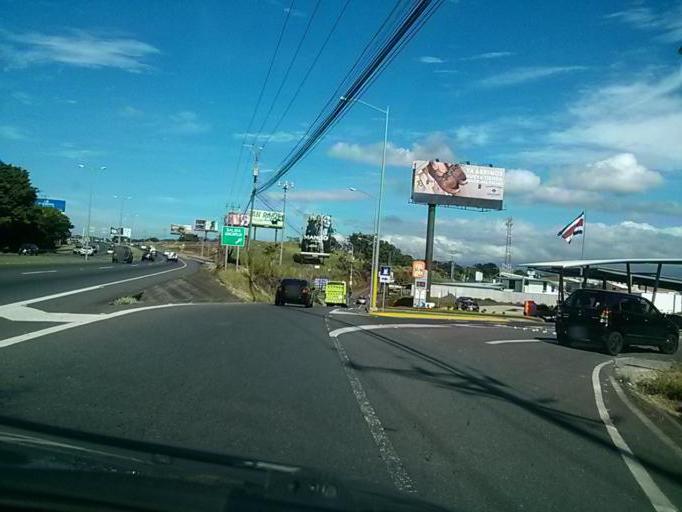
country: CR
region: San Jose
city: San Rafael
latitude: 9.9460
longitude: -84.1511
